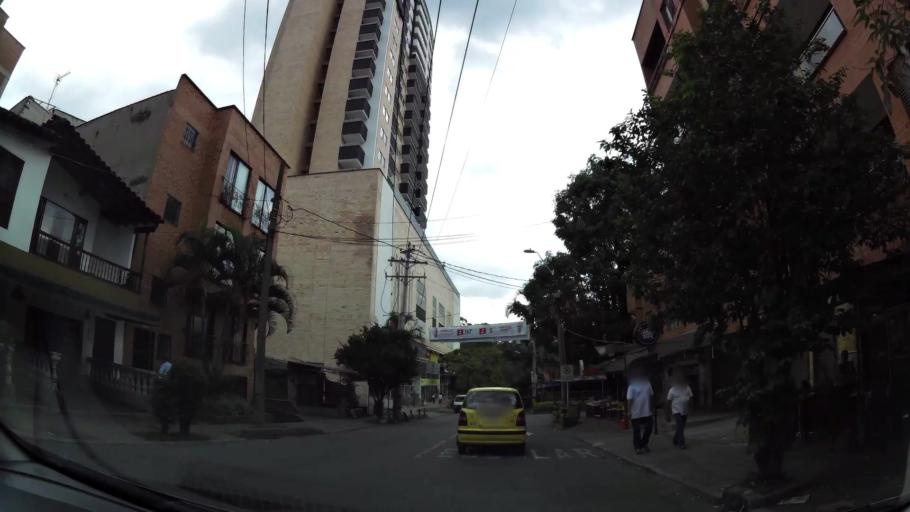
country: CO
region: Antioquia
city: Envigado
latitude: 6.1603
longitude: -75.5950
